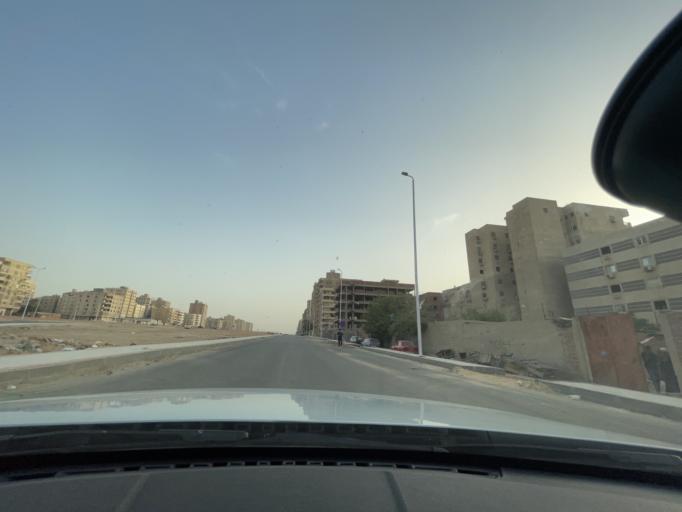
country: EG
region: Muhafazat al Qahirah
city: Cairo
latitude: 30.0562
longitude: 31.3730
